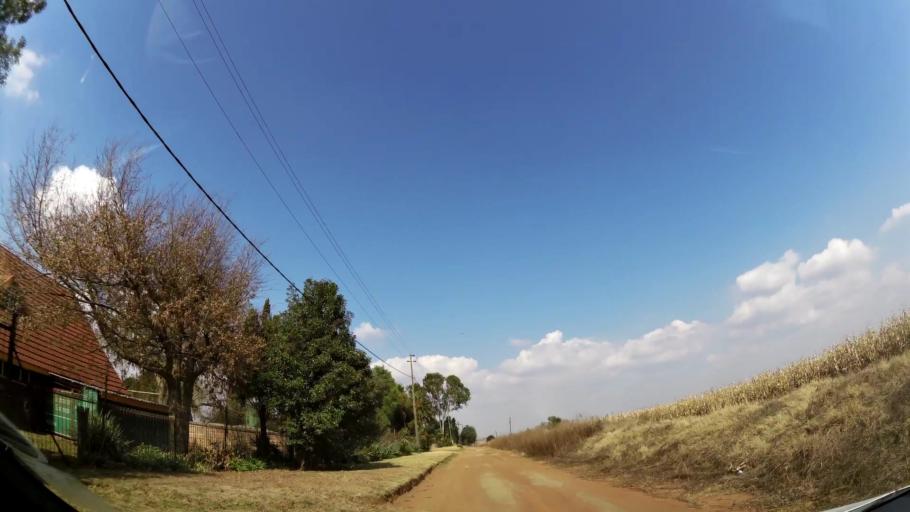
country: ZA
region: Gauteng
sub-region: Ekurhuleni Metropolitan Municipality
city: Springs
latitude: -26.1943
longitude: 28.5328
